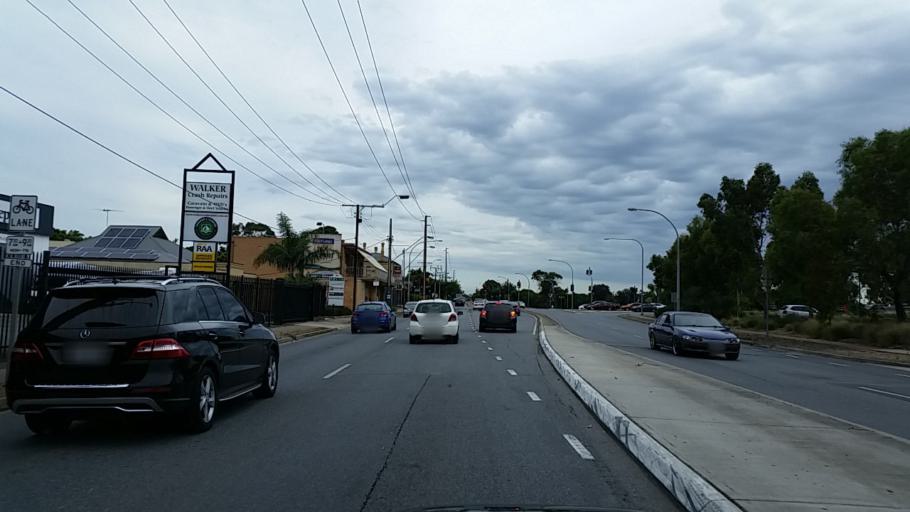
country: AU
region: South Australia
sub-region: Prospect
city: Prospect
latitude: -34.8732
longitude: 138.5840
